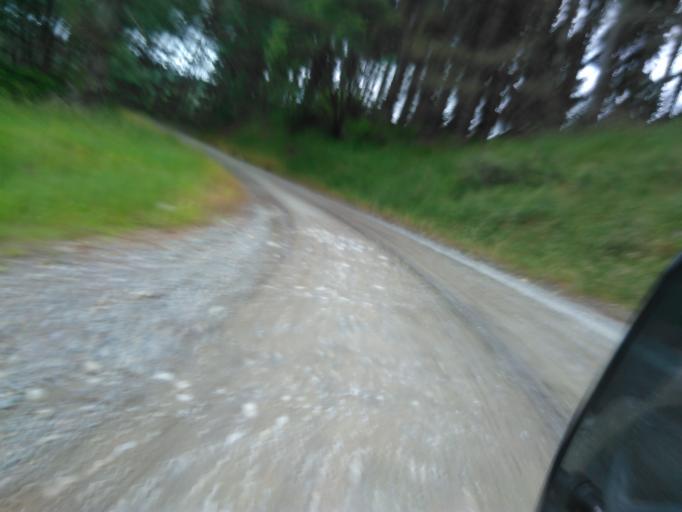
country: NZ
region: Gisborne
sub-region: Gisborne District
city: Gisborne
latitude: -38.0494
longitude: 178.1247
